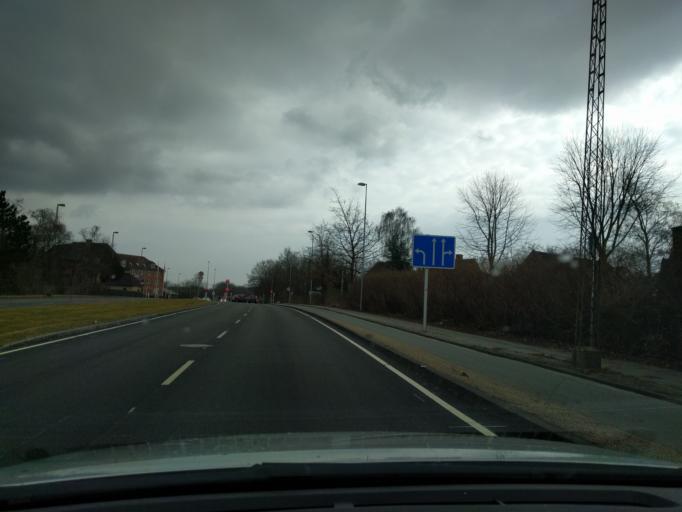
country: DK
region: South Denmark
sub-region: Odense Kommune
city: Odense
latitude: 55.3912
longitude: 10.3471
